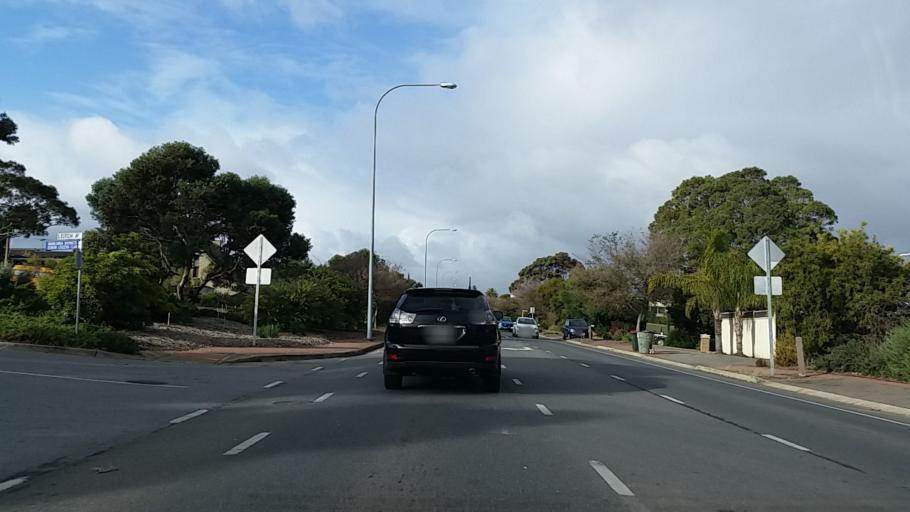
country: AU
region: South Australia
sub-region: Adelaide
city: Port Noarlunga
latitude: -35.1463
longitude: 138.4805
